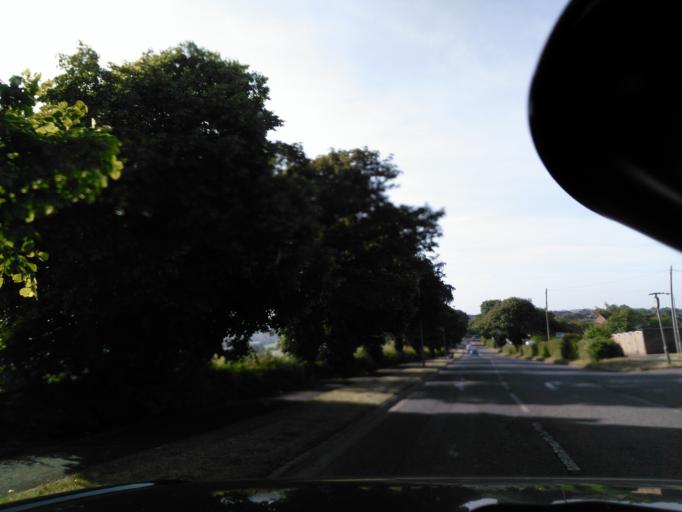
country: GB
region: England
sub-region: Wiltshire
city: Woodford
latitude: 51.0899
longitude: -1.8265
